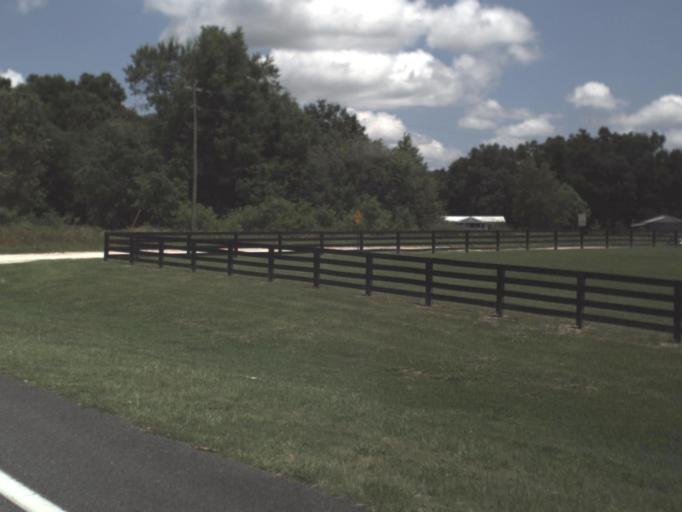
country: US
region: Florida
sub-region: Alachua County
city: High Springs
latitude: 29.8925
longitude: -82.6768
